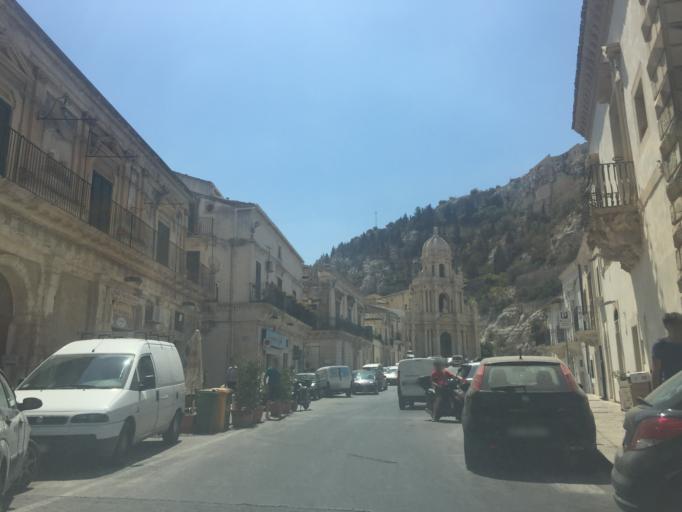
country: IT
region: Sicily
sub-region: Ragusa
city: Scicli
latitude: 36.7923
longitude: 14.7076
